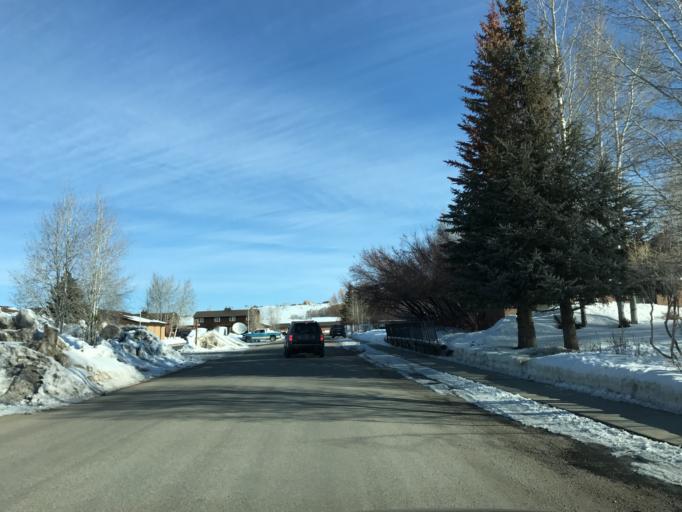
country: US
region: Wyoming
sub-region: Sublette County
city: Pinedale
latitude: 42.8682
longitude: -109.8572
